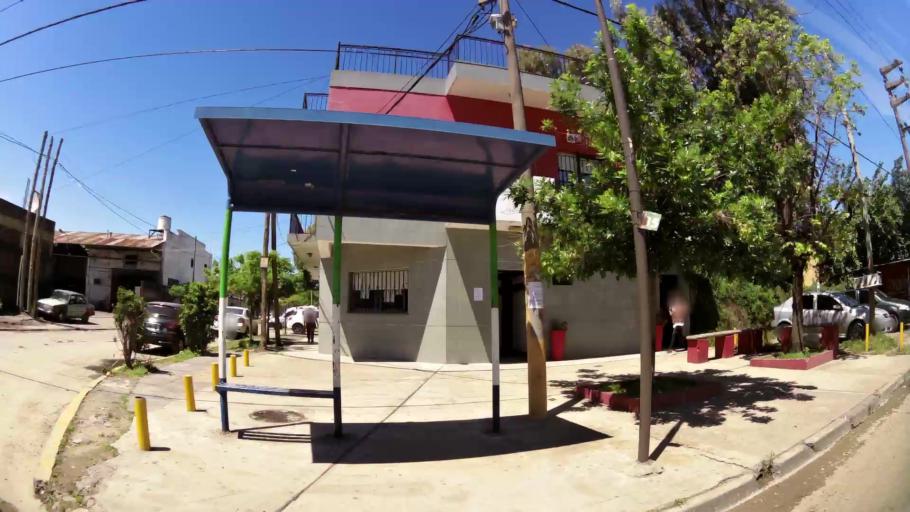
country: AR
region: Buenos Aires
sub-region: Partido de Quilmes
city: Quilmes
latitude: -34.7352
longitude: -58.2939
